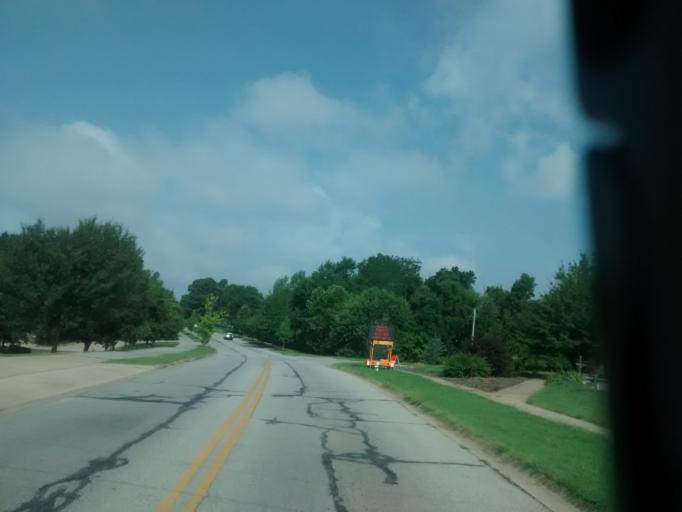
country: US
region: Arkansas
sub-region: Washington County
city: Fayetteville
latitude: 36.0559
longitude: -94.1509
